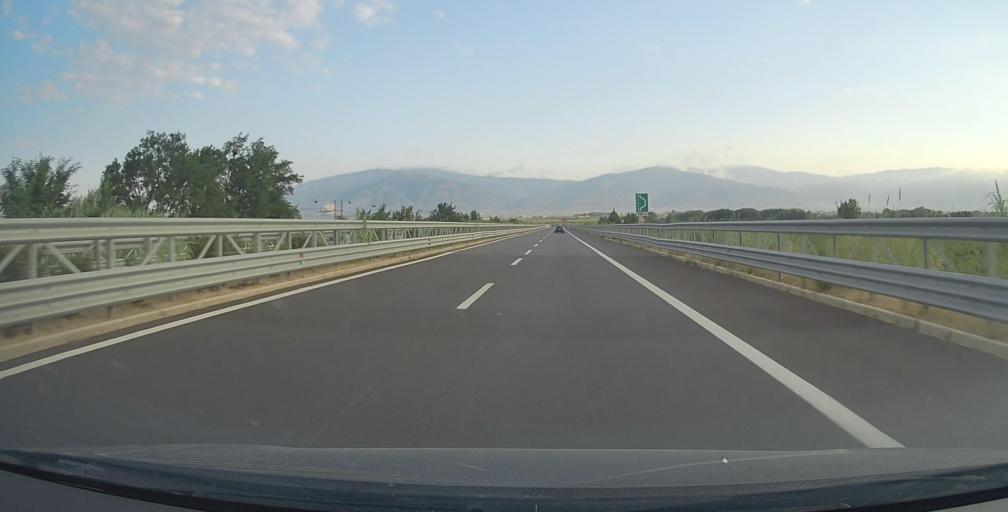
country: IT
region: Calabria
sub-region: Provincia di Catanzaro
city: Santa Eufemia Lamezia
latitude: 38.8966
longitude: 16.2792
